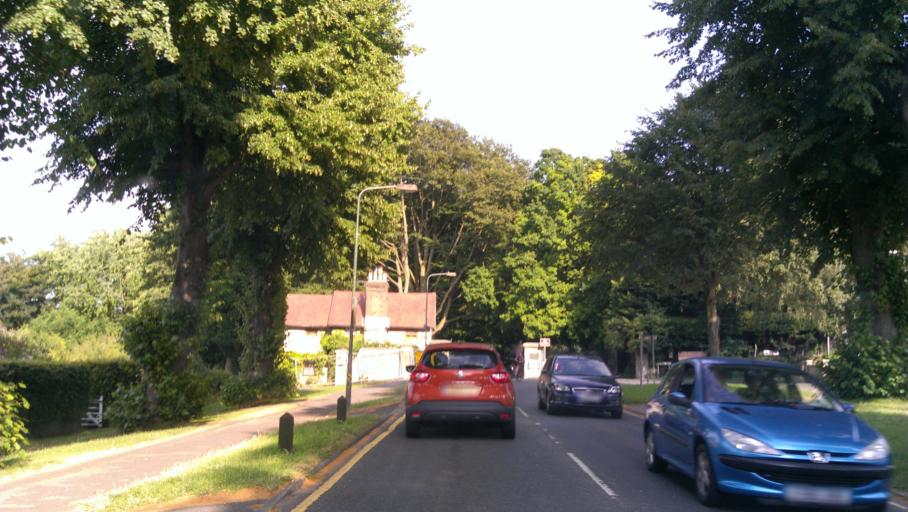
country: GB
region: England
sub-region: Kent
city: Maidstone
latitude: 51.2703
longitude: 0.5343
